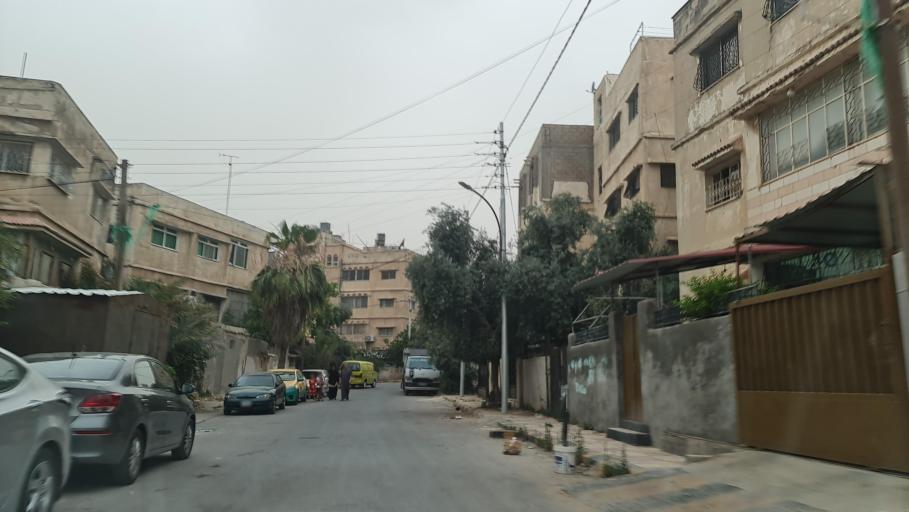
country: JO
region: Amman
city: Amman
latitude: 31.9345
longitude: 35.9346
